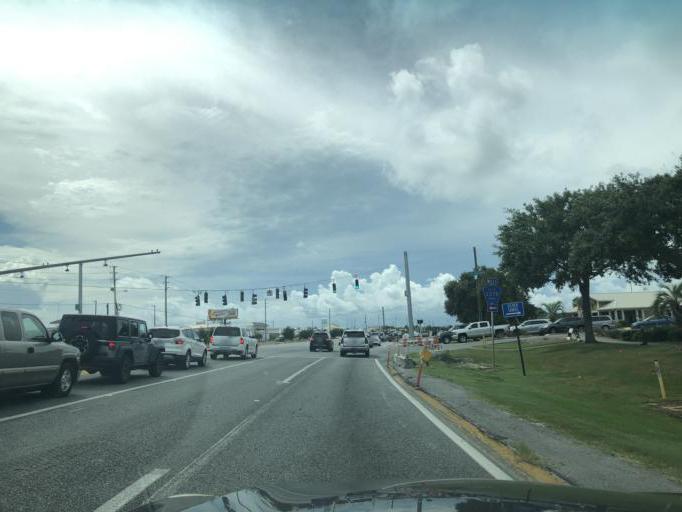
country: US
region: Florida
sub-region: Walton County
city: Miramar Beach
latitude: 30.3768
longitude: -86.3484
